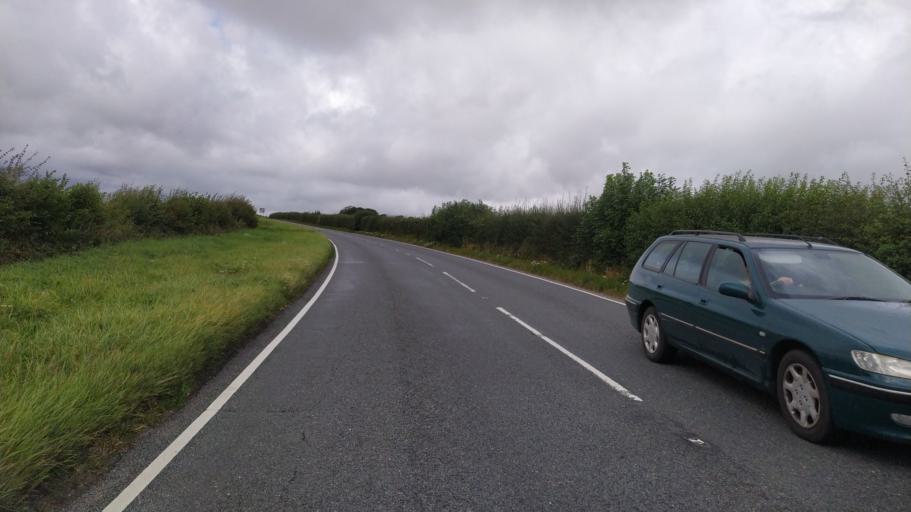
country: GB
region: England
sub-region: Hampshire
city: Kings Worthy
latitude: 51.0449
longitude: -1.2386
